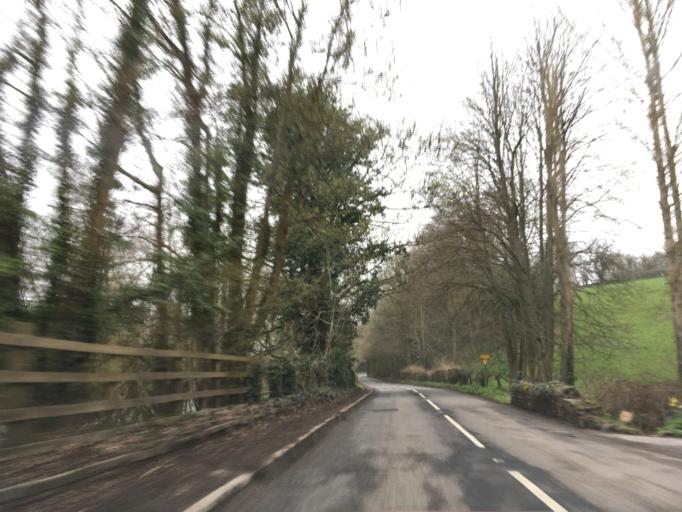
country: GB
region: Wales
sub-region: Monmouthshire
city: Usk
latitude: 51.7124
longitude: -2.9099
